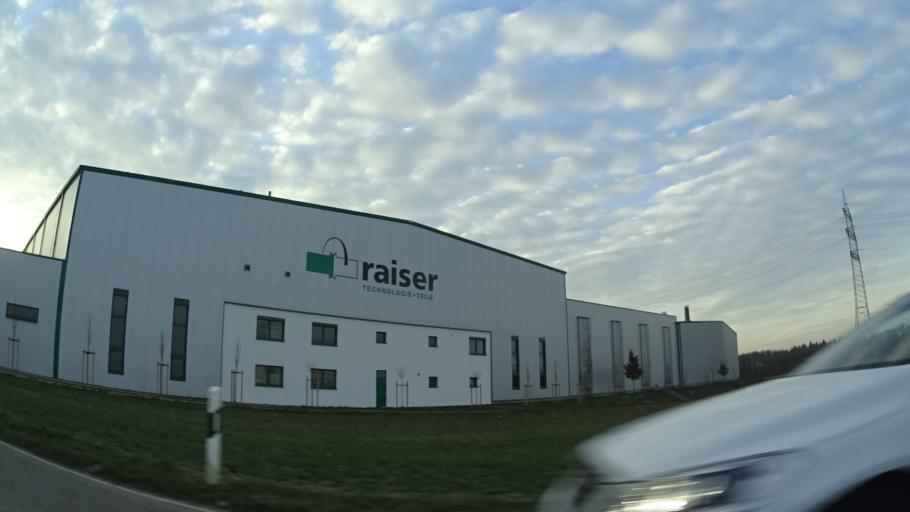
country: DE
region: Baden-Wuerttemberg
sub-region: Regierungsbezirk Stuttgart
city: Hemmingen
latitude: 48.8925
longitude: 9.0077
